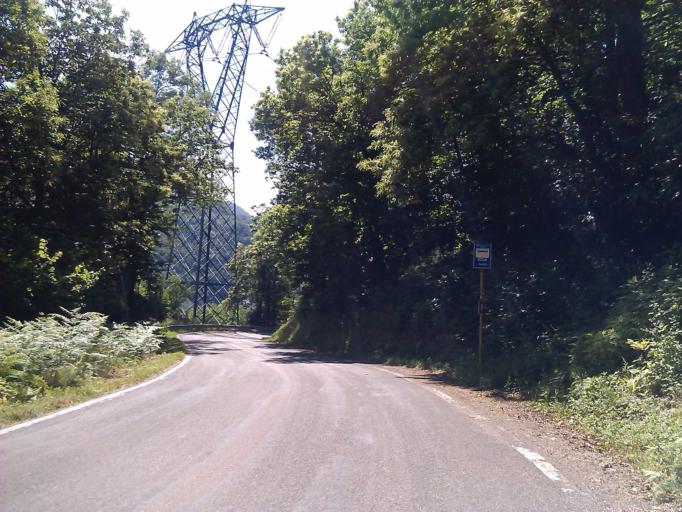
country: IT
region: Tuscany
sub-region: Provincia di Pistoia
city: Sambuca Pistoiese
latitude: 44.1022
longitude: 11.0436
